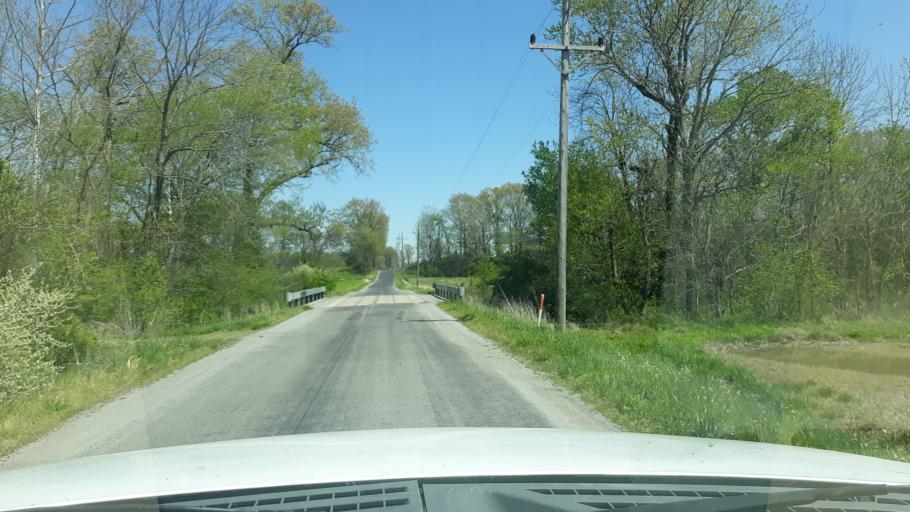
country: US
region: Illinois
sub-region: Saline County
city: Harrisburg
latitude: 37.8341
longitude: -88.6194
